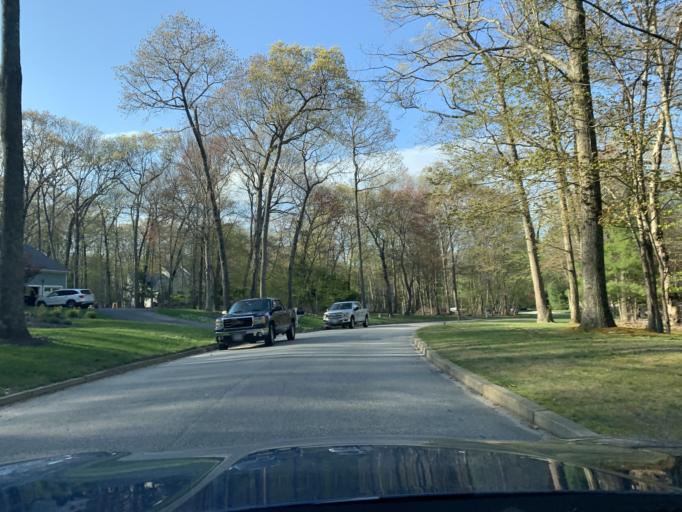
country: US
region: Rhode Island
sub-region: Washington County
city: Exeter
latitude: 41.6073
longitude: -71.5325
